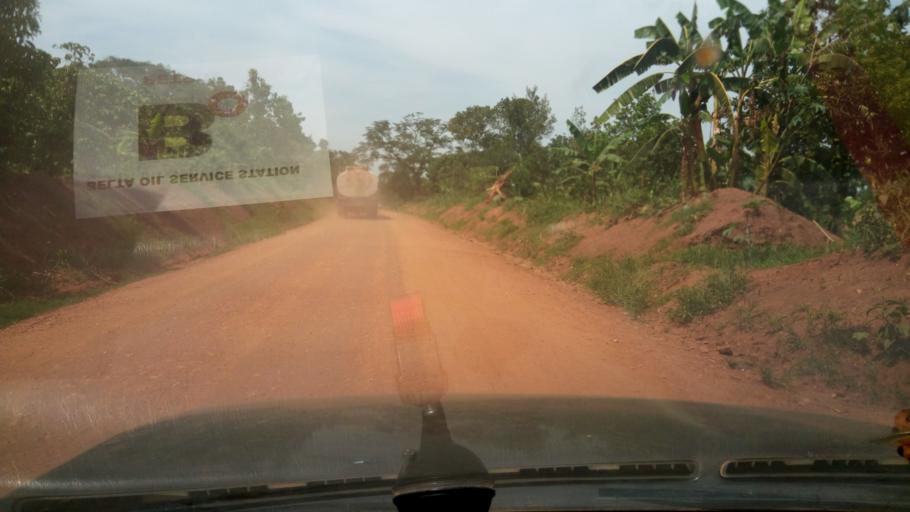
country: UG
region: Central Region
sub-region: Mityana District
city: Mityana
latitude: 0.4954
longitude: 32.1276
